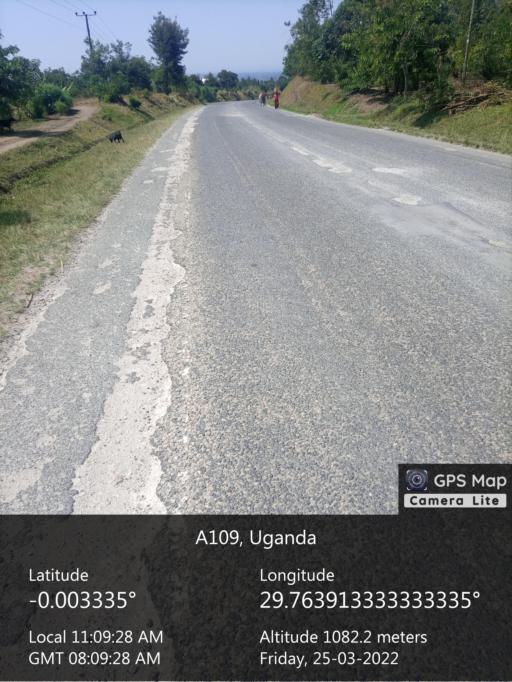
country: UG
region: Western Region
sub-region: Kasese District
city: Kilembe
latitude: -0.0033
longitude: 29.7639
